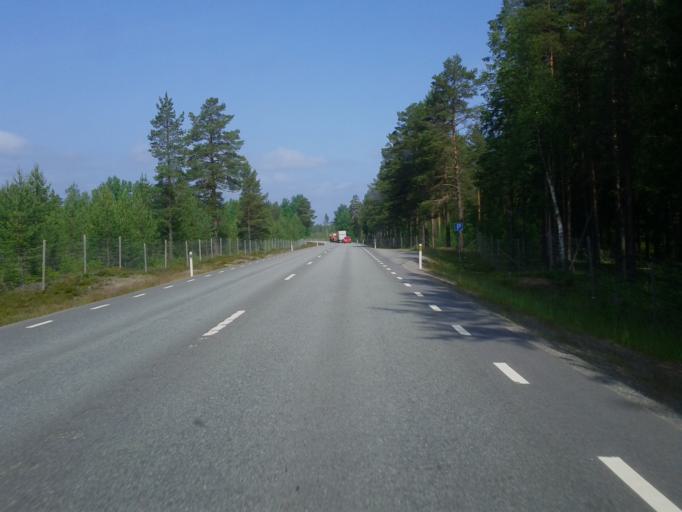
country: SE
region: Vaesterbotten
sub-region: Skelleftea Kommun
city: Burea
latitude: 64.5833
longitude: 21.2198
